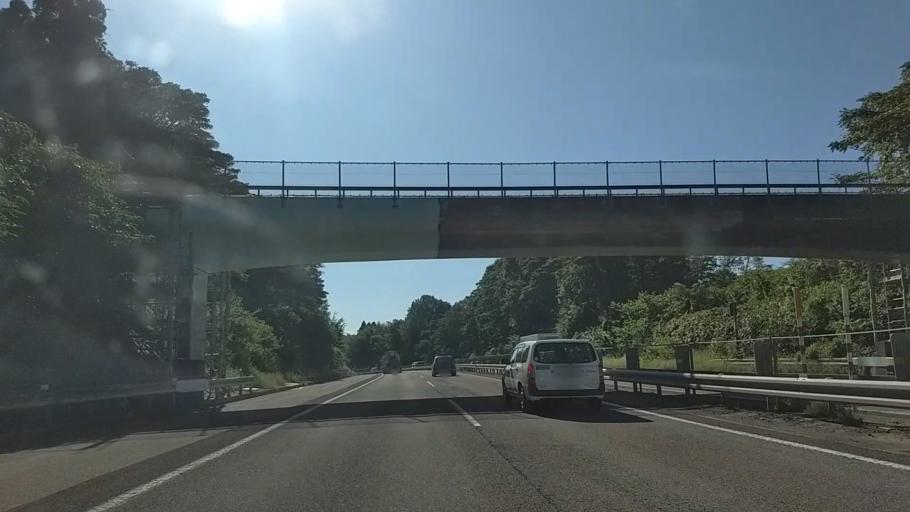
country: JP
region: Ishikawa
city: Tsubata
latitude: 36.6000
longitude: 136.7327
